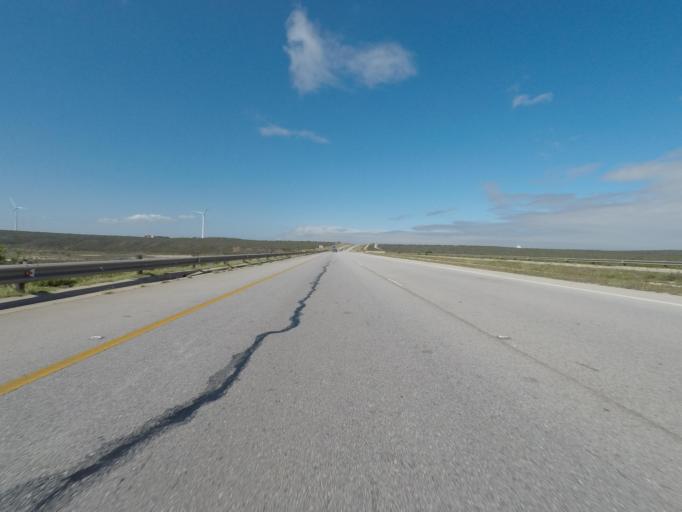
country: ZA
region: Eastern Cape
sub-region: Nelson Mandela Bay Metropolitan Municipality
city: Port Elizabeth
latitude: -33.7704
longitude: 25.6726
